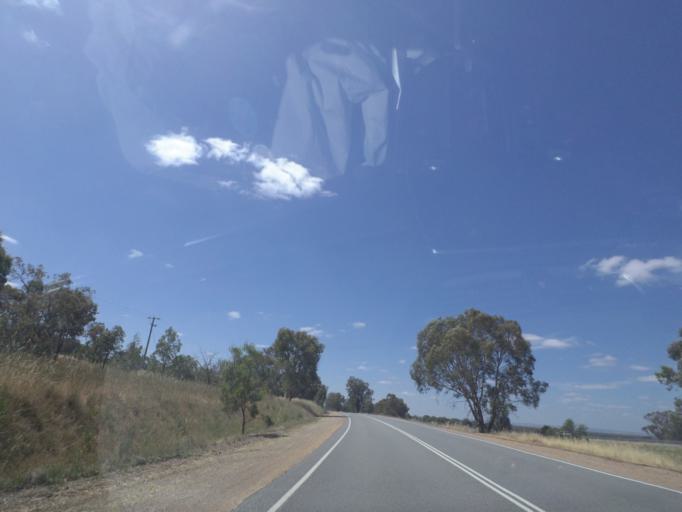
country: AU
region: Victoria
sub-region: Wangaratta
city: Wangaratta
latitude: -36.4584
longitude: 146.2357
